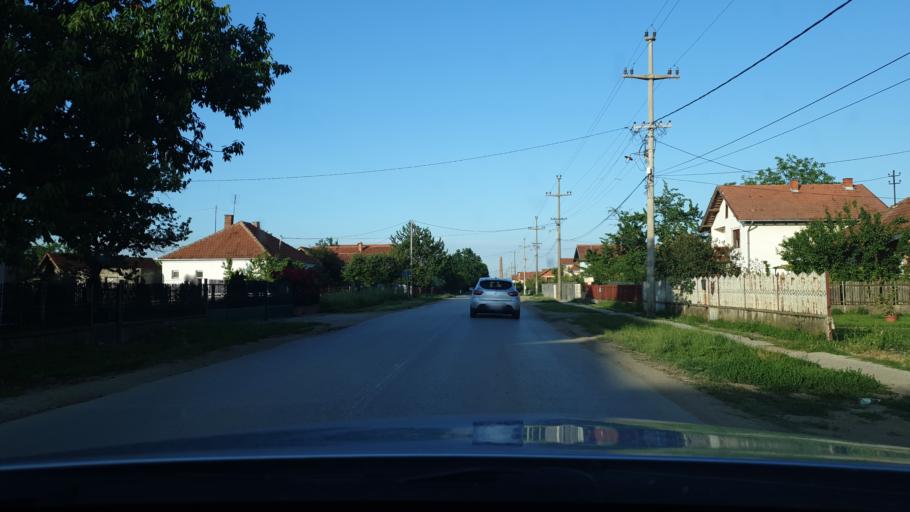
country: RS
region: Central Serbia
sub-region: Podunavski Okrug
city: Velika Plana
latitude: 44.3408
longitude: 21.0934
